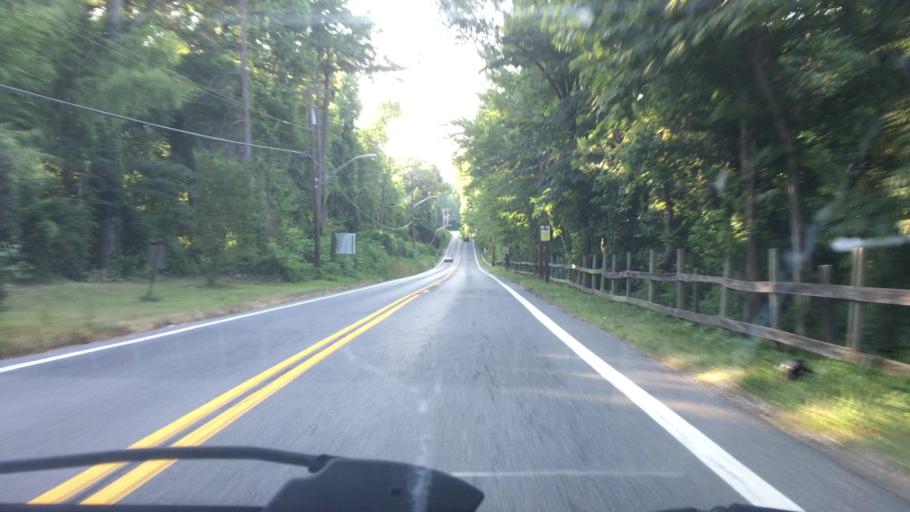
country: US
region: Maryland
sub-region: Prince George's County
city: Glenn Dale
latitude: 39.0139
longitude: -76.7822
